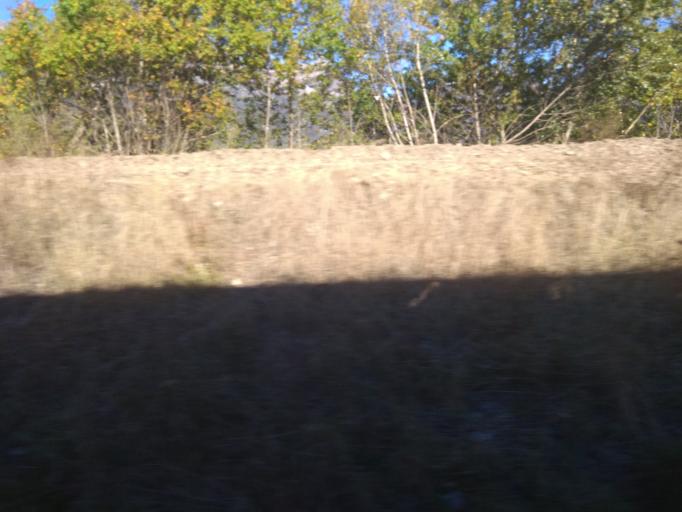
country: FR
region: Rhone-Alpes
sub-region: Departement de la Haute-Savoie
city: Passy
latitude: 45.9075
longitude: 6.6914
